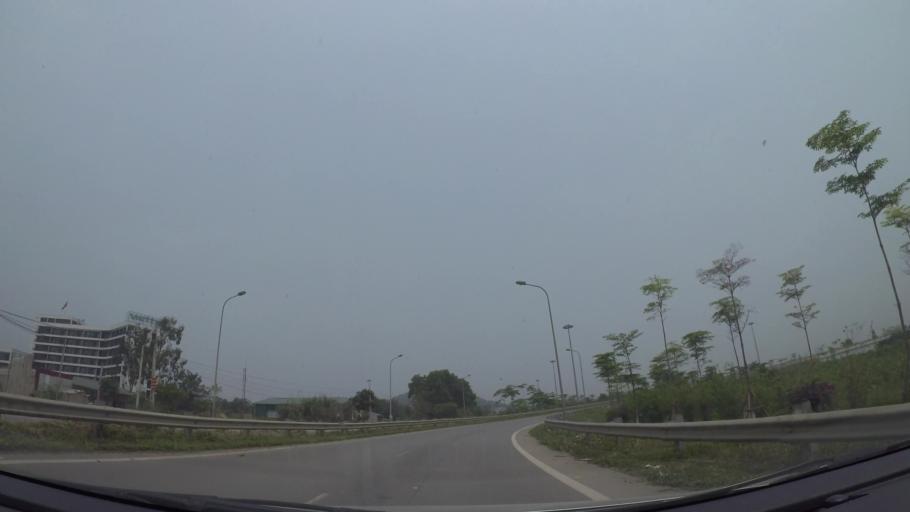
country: VN
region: Ha Noi
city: Lien Quan
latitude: 20.9882
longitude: 105.5227
